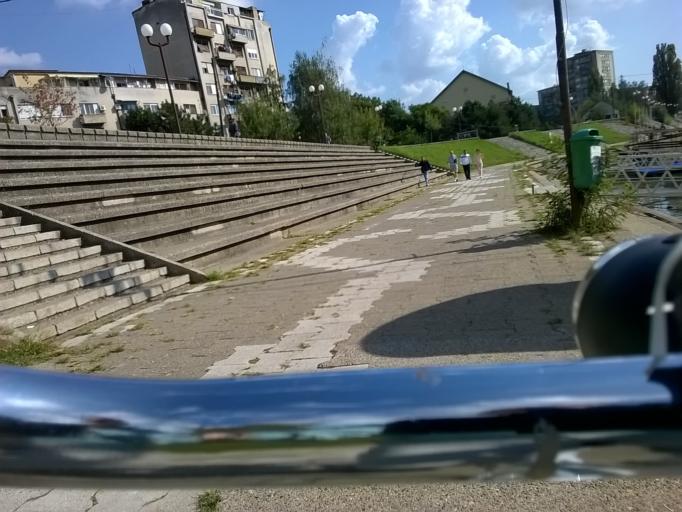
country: RS
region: Autonomna Pokrajina Vojvodina
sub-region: Juznobanatski Okrug
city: Pancevo
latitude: 44.8667
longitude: 20.6389
